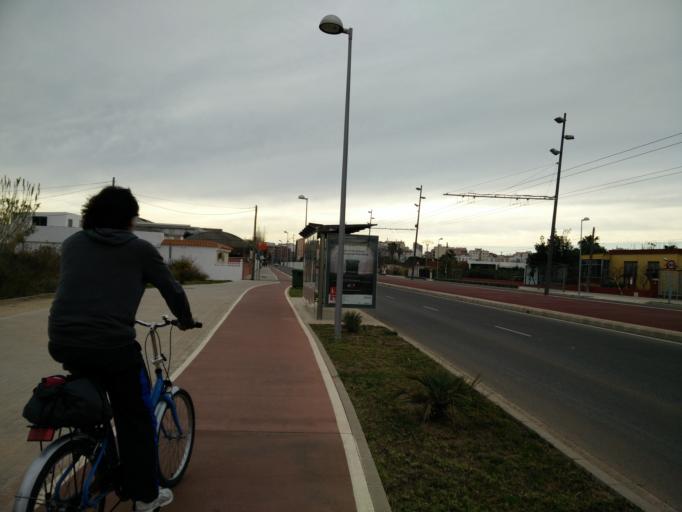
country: ES
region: Valencia
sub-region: Provincia de Castello
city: Castello de la Plana
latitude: 39.9778
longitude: 0.0056
